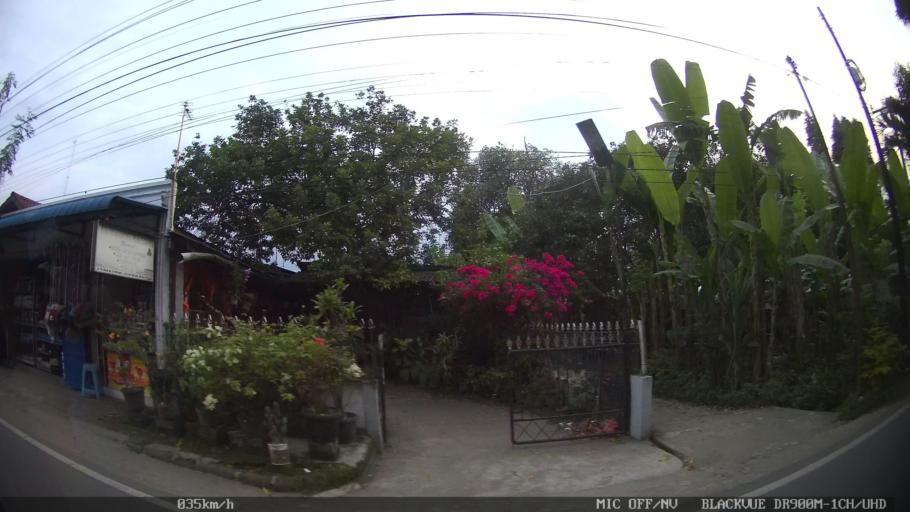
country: ID
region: North Sumatra
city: Sunggal
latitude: 3.5833
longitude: 98.6006
